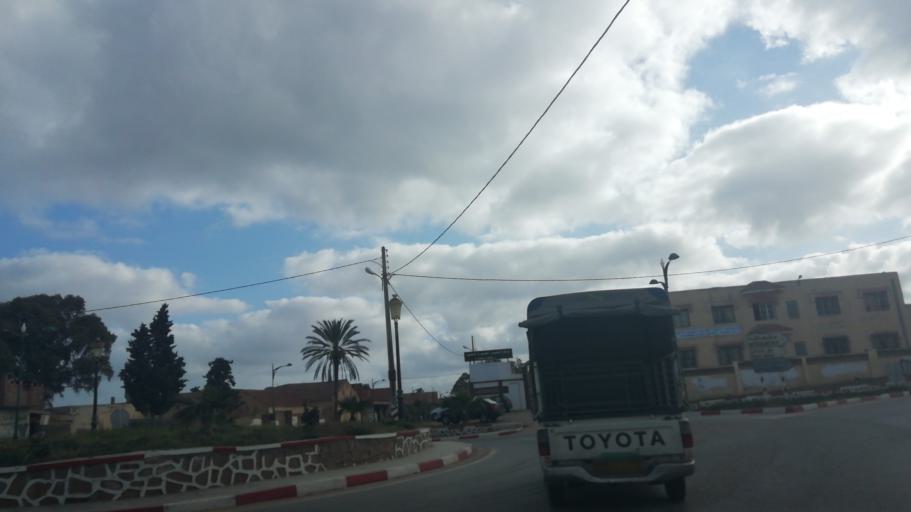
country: DZ
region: Relizane
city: Mazouna
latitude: 36.2627
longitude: 0.6150
